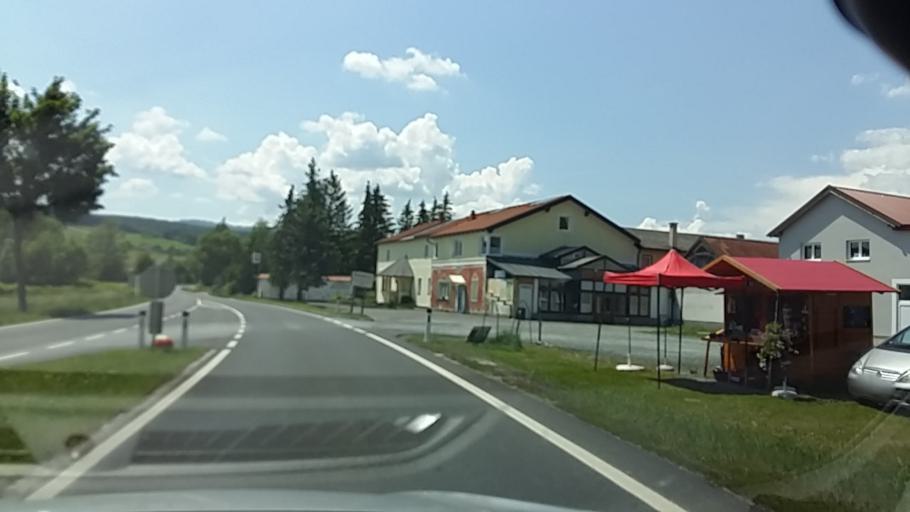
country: AT
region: Burgenland
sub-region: Politischer Bezirk Oberpullendorf
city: Lockenhaus
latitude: 47.4106
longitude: 16.3820
